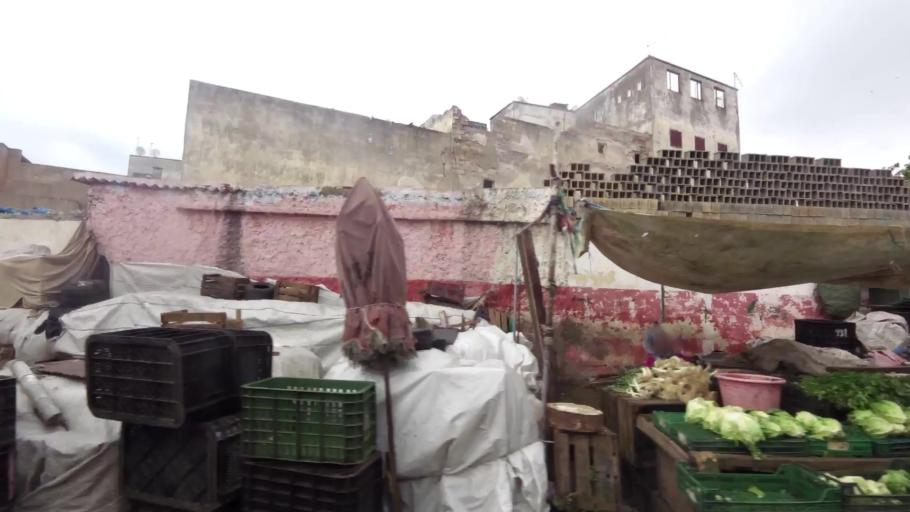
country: MA
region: Grand Casablanca
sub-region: Casablanca
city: Casablanca
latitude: 33.5995
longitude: -7.6277
